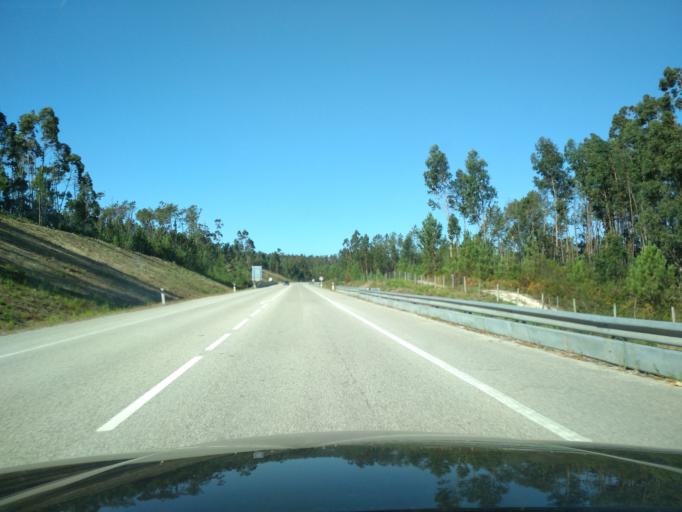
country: PT
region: Leiria
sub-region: Pombal
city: Lourical
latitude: 39.9874
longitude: -8.7462
